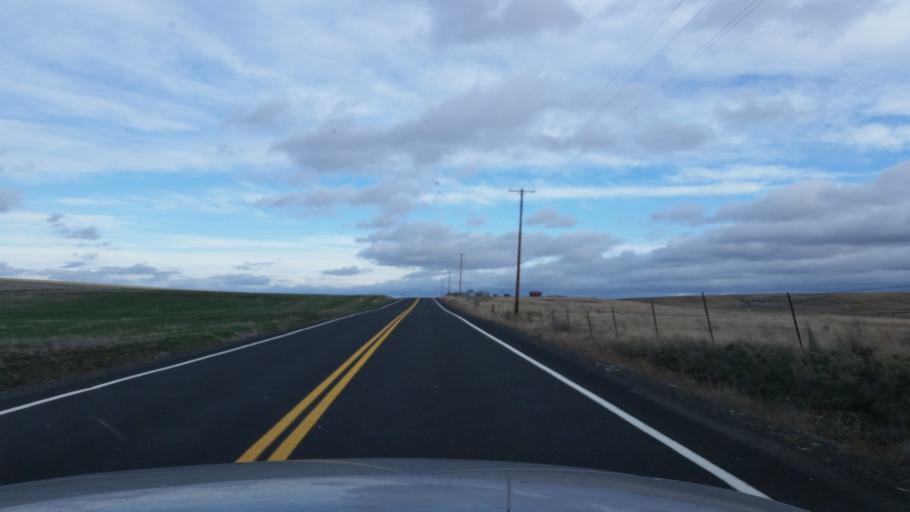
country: US
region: Washington
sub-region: Lincoln County
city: Davenport
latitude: 47.3500
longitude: -118.0740
